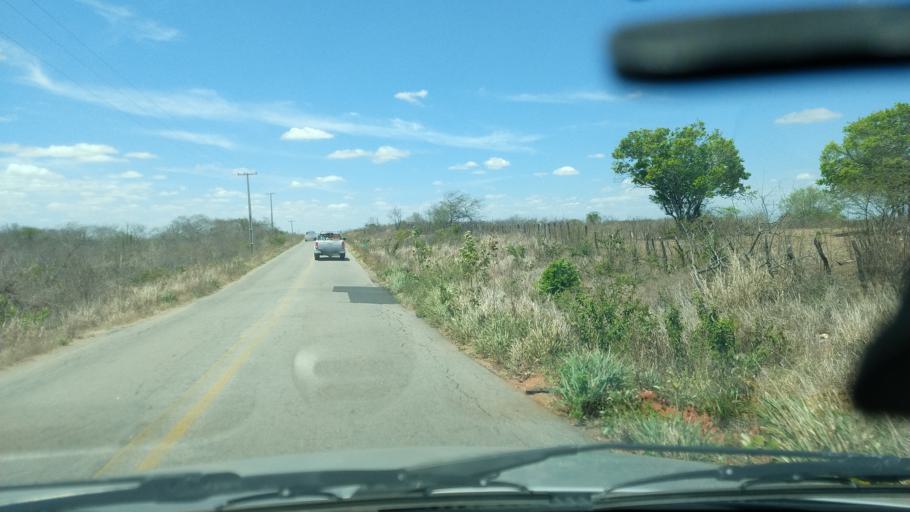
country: BR
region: Rio Grande do Norte
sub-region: Sao Paulo Do Potengi
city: Sao Paulo do Potengi
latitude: -5.9096
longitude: -35.5984
